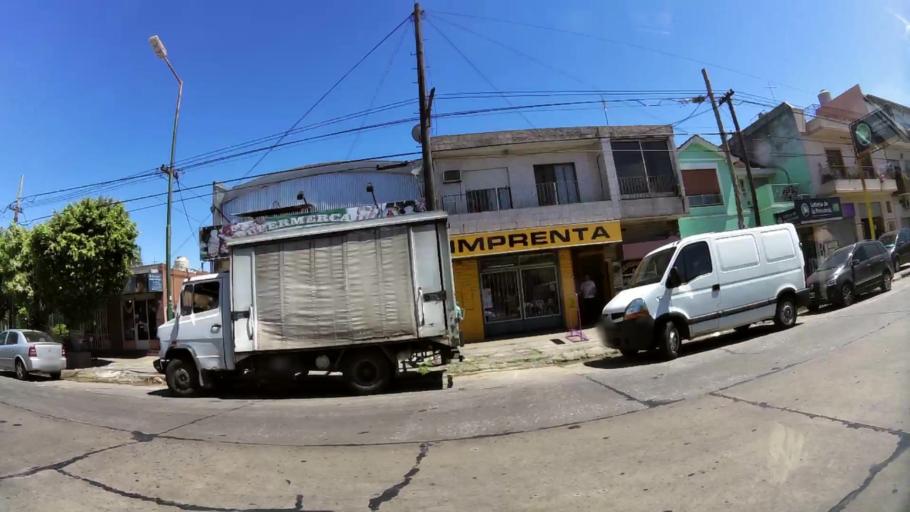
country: AR
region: Buenos Aires
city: Caseros
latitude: -34.5890
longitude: -58.5633
